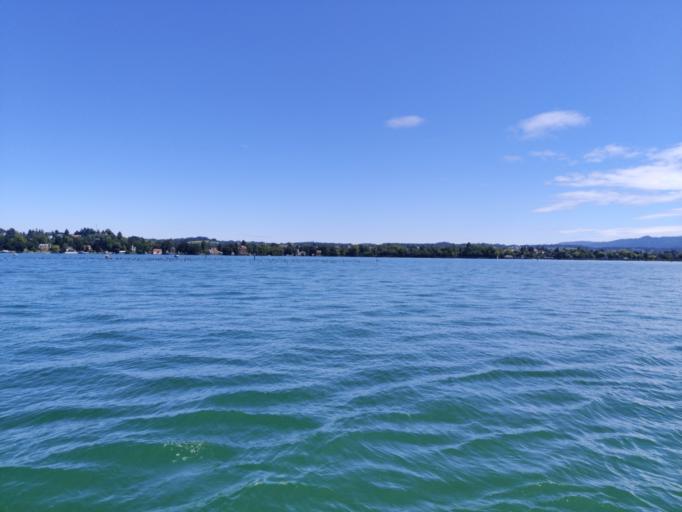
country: DE
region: Bavaria
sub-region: Swabia
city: Lindau
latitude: 47.5468
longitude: 9.6666
